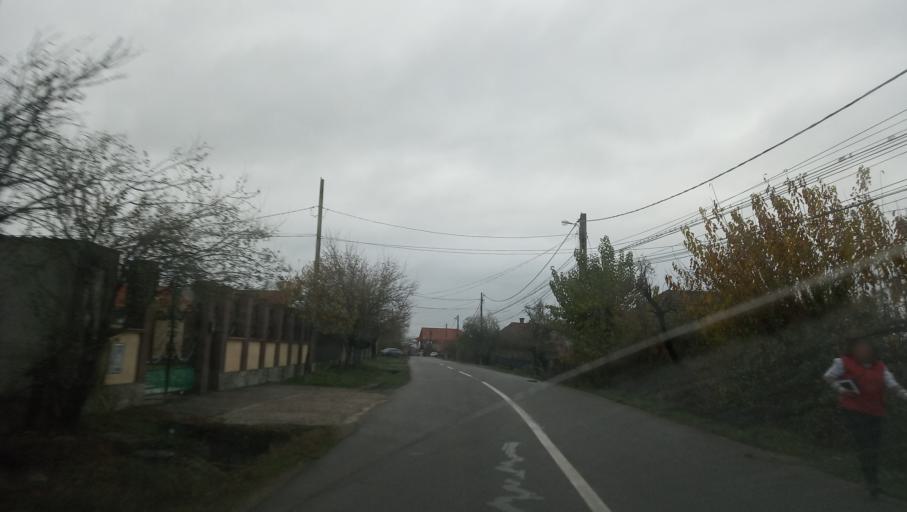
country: RO
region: Gorj
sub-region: Comuna Bumbesti-Jiu
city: Bumbesti-Jiu
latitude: 45.1350
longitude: 23.3893
